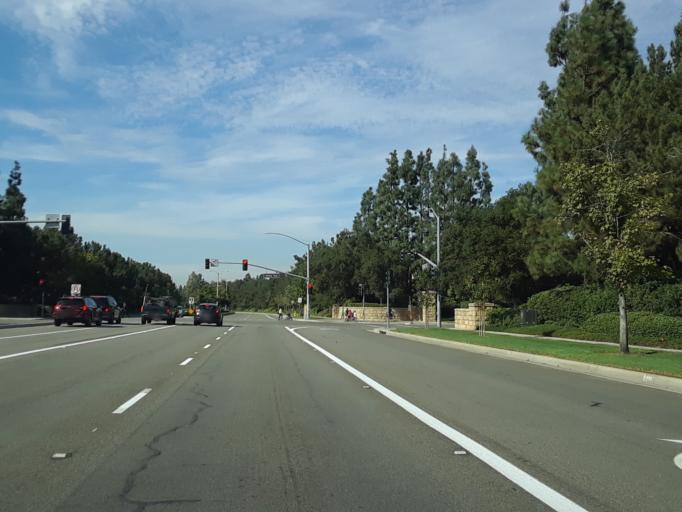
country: US
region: California
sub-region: Orange County
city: Irvine
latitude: 33.6631
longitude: -117.7780
